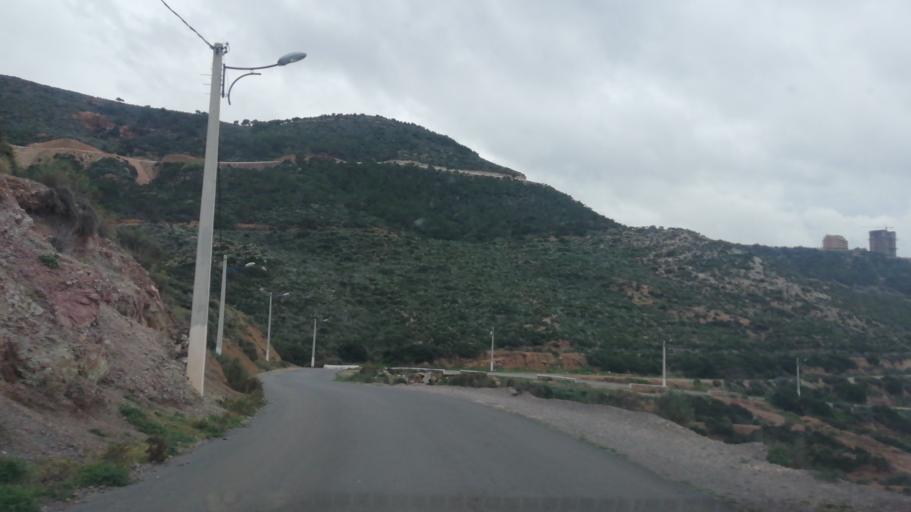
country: DZ
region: Oran
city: Bir el Djir
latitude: 35.7685
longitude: -0.5242
